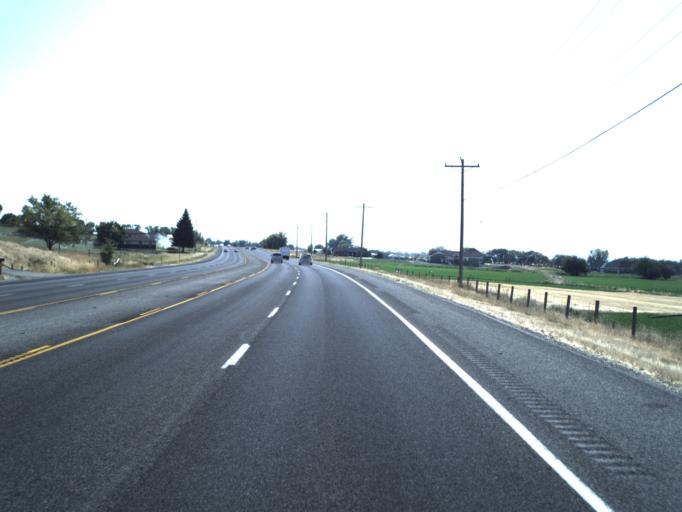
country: US
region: Utah
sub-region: Cache County
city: Smithfield
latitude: 41.8707
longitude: -111.8275
